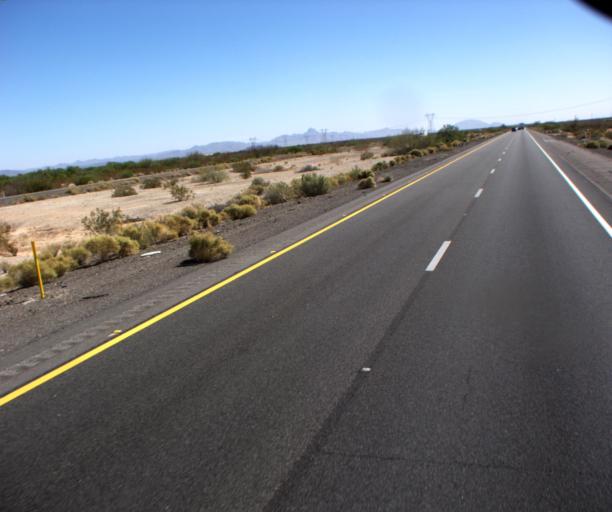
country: US
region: Arizona
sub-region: La Paz County
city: Salome
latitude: 33.5772
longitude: -113.4092
